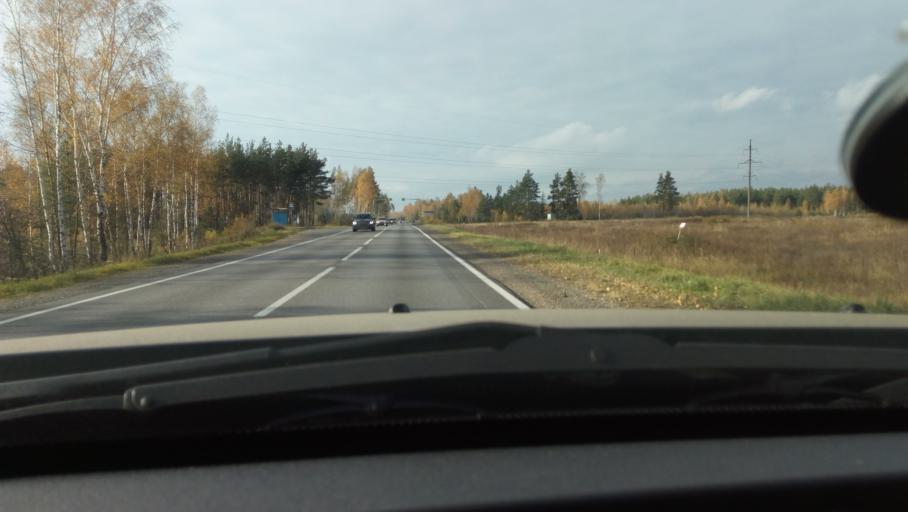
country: RU
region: Moskovskaya
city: Fryazevo
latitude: 55.7424
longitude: 38.5311
